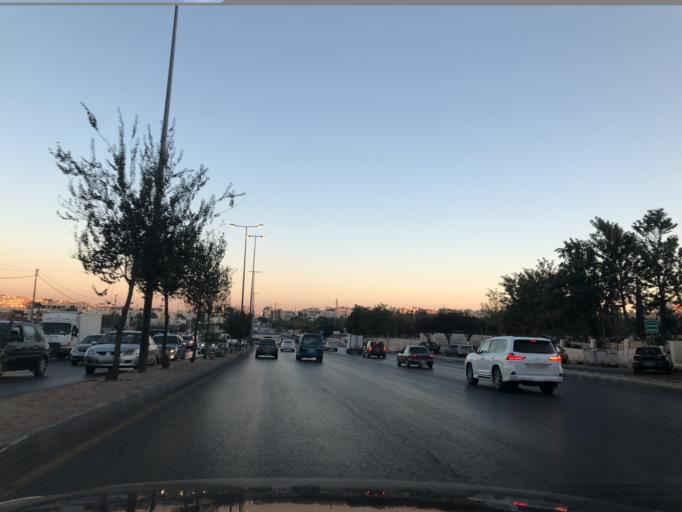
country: JO
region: Amman
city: Wadi as Sir
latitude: 31.9772
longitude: 35.8377
